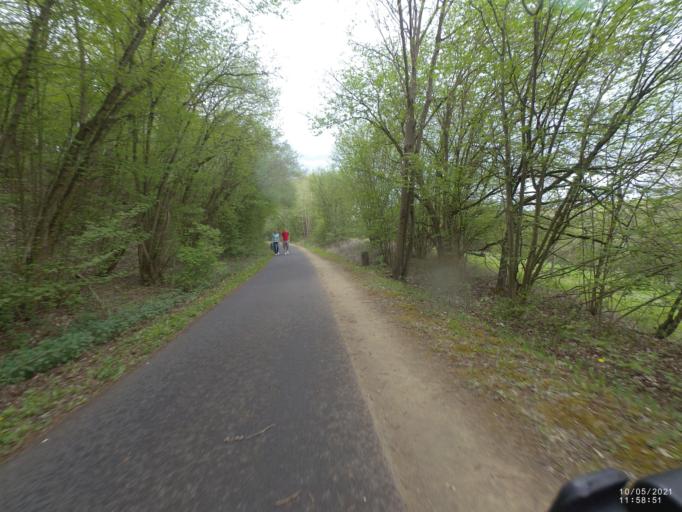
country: DE
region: Rheinland-Pfalz
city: Kerben
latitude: 50.3206
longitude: 7.3664
